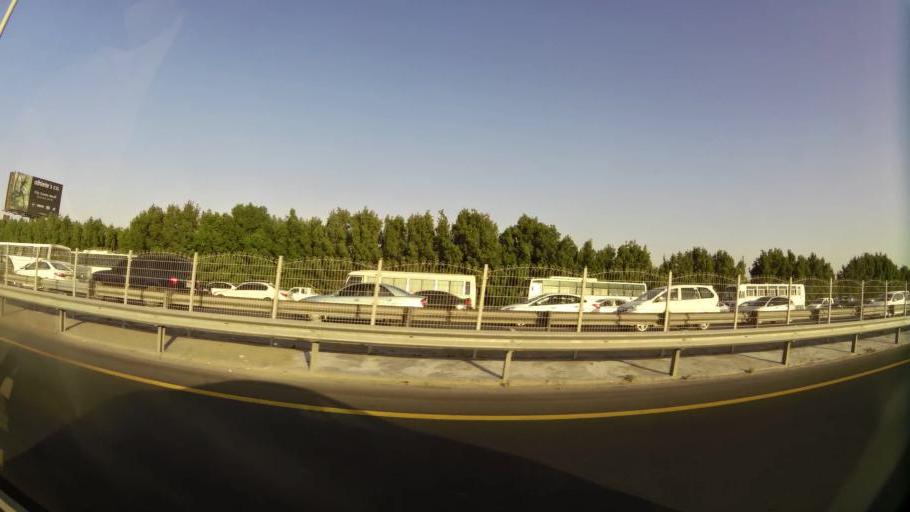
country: AE
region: Ash Shariqah
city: Sharjah
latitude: 25.2662
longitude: 55.4115
